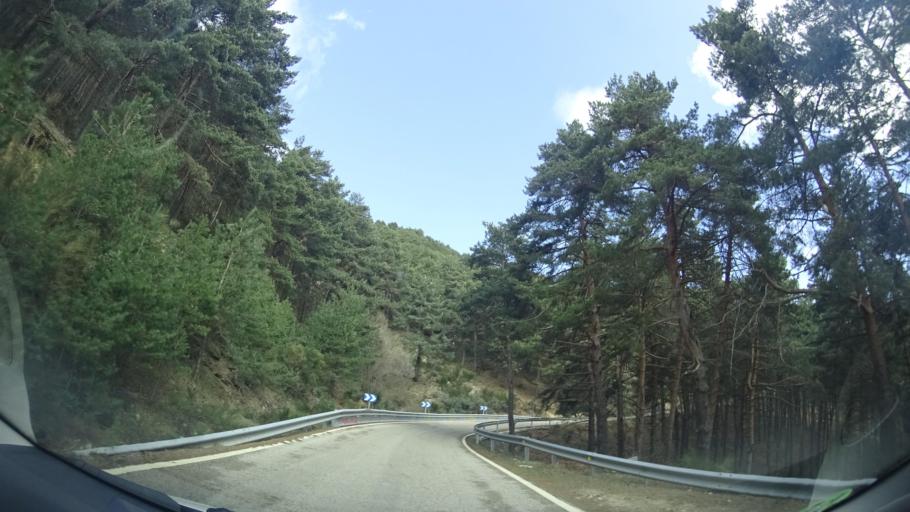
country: ES
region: Madrid
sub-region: Provincia de Madrid
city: Miraflores de la Sierra
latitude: 40.8629
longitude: -3.7643
